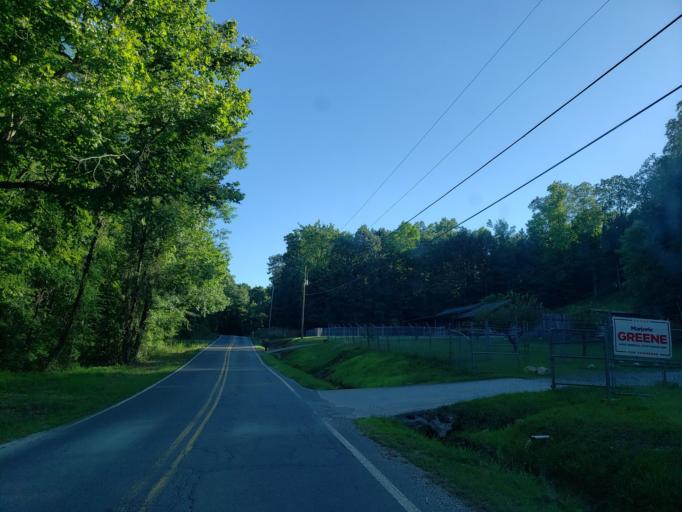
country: US
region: Georgia
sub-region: Floyd County
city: Shannon
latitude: 34.3853
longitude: -85.1260
